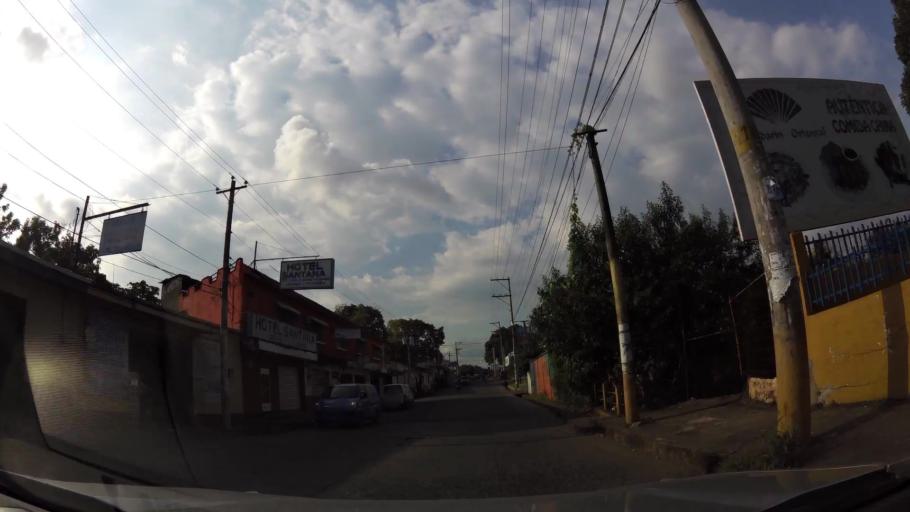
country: GT
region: Retalhuleu
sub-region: Municipio de Retalhuleu
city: Retalhuleu
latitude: 14.5391
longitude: -91.6743
